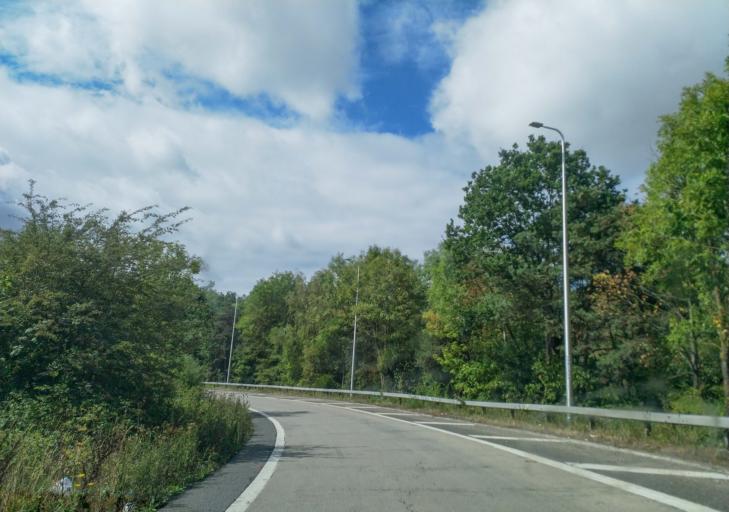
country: GB
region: England
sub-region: Wokingham
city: Winnersh
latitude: 51.4317
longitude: -0.8581
